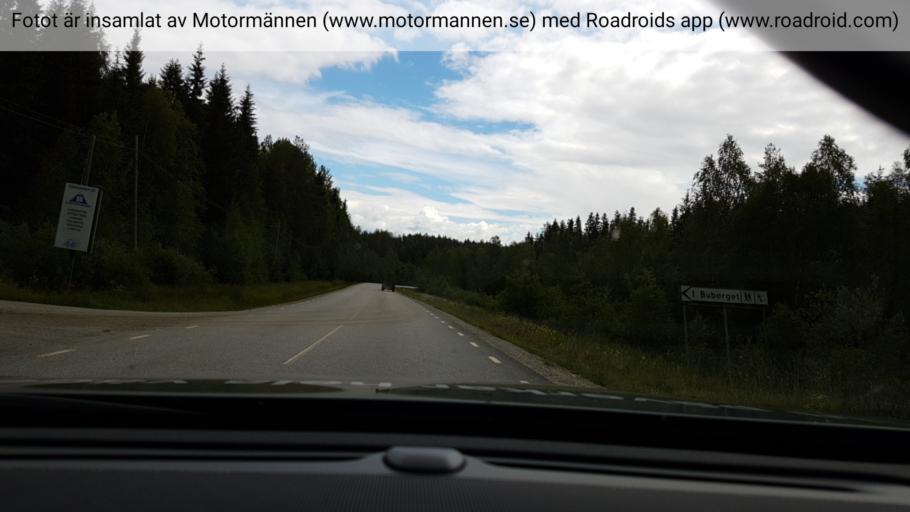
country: SE
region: Vaesterbotten
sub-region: Vindelns Kommun
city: Vindeln
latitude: 64.2066
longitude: 19.6790
